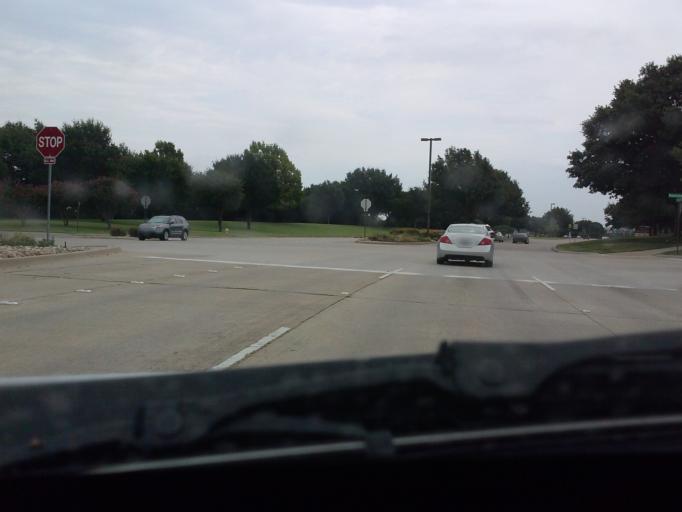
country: US
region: Texas
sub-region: Denton County
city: The Colony
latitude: 33.0701
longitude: -96.8106
